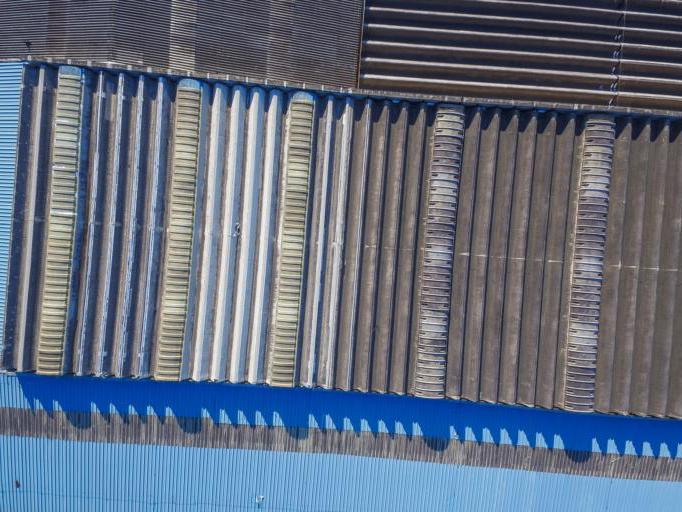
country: BR
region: Sao Paulo
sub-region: Jacarei
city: Jacarei
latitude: -23.2939
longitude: -45.9309
